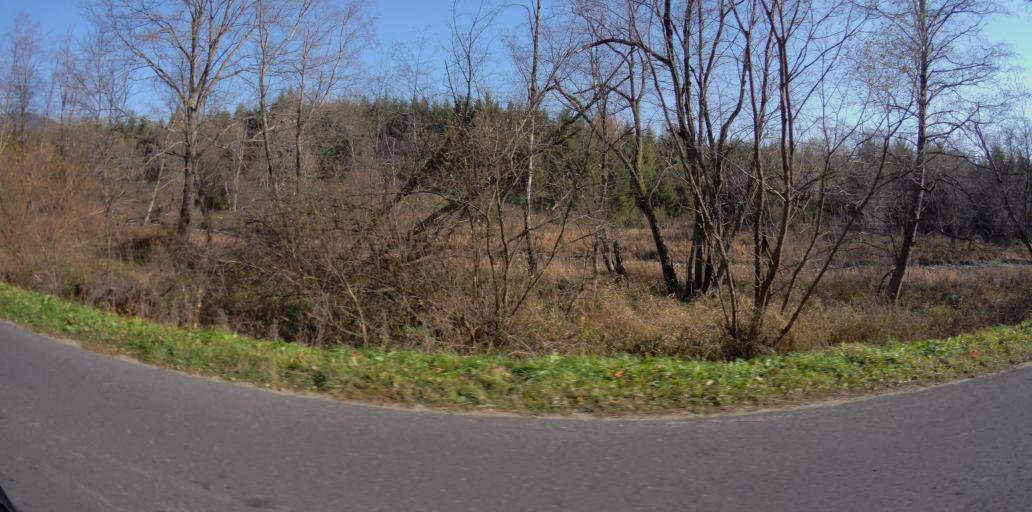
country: PL
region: Subcarpathian Voivodeship
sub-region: Powiat bieszczadzki
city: Lutowiska
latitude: 49.1804
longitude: 22.6819
